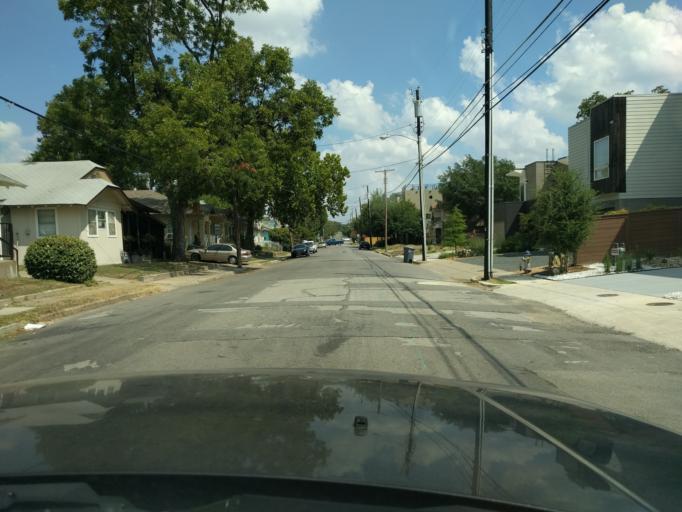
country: US
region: Texas
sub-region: Dallas County
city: Dallas
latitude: 32.8019
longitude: -96.7849
